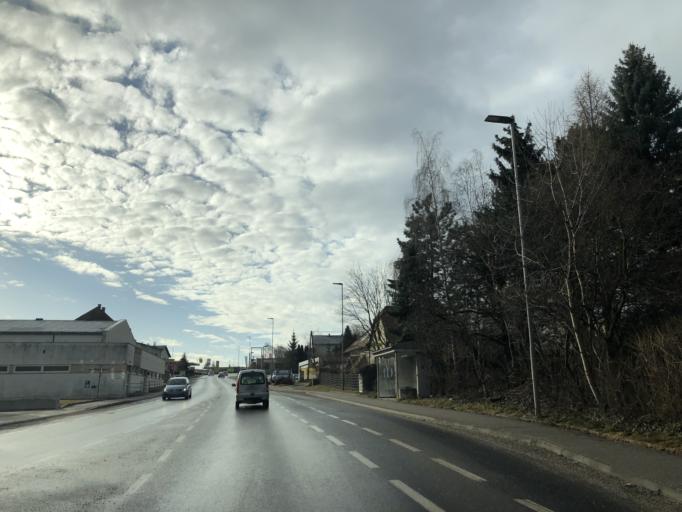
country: AT
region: Upper Austria
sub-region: Politischer Bezirk Freistadt
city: Freistadt
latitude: 48.5011
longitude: 14.5020
